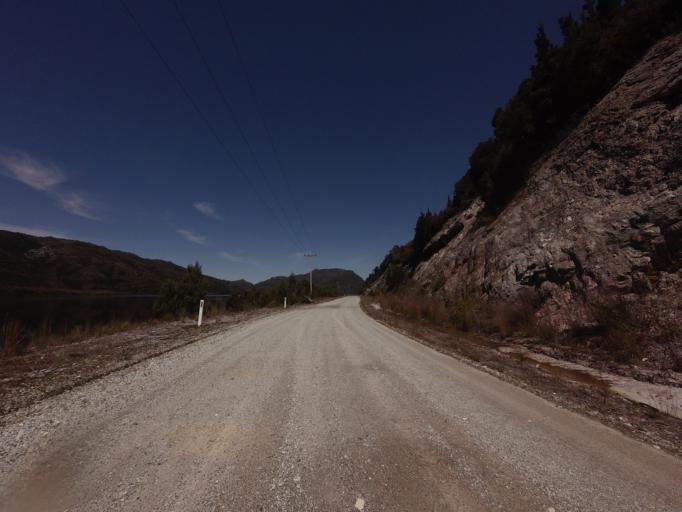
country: AU
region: Tasmania
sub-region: West Coast
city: Queenstown
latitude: -42.7718
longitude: 145.9847
